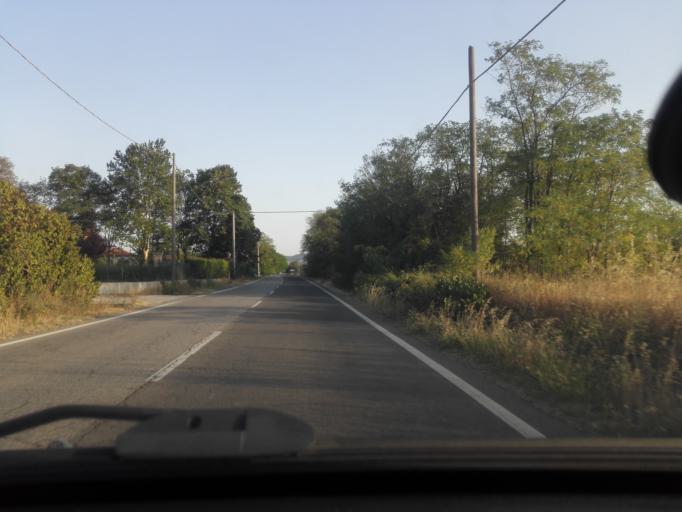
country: IT
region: Piedmont
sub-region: Provincia di Alessandria
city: Cassano Spinola
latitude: 44.7612
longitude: 8.8396
